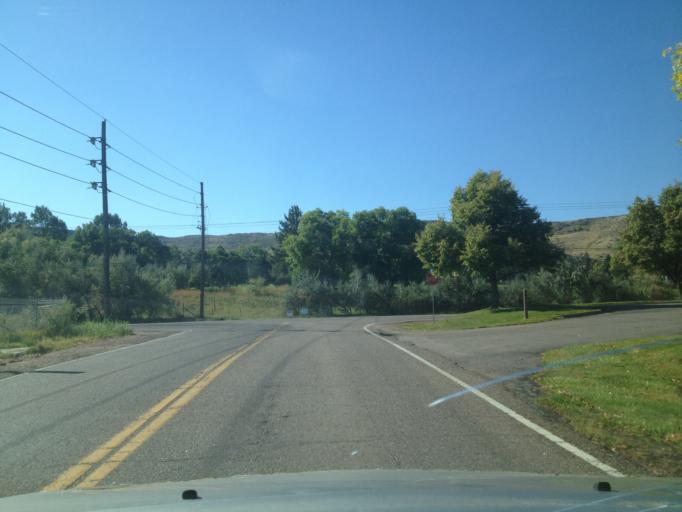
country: US
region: Colorado
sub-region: Jefferson County
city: Applewood
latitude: 39.7617
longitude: -105.1749
